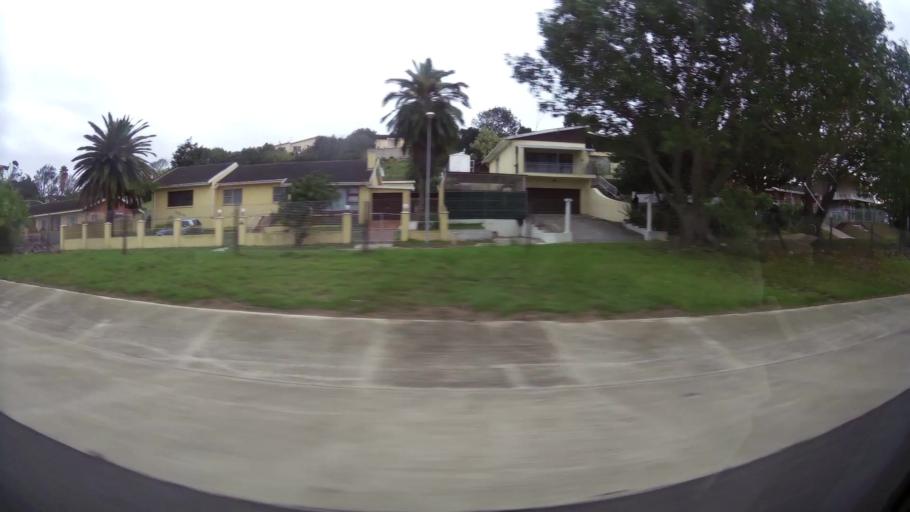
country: ZA
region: Eastern Cape
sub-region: Nelson Mandela Bay Metropolitan Municipality
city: Port Elizabeth
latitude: -33.9359
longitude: 25.5559
